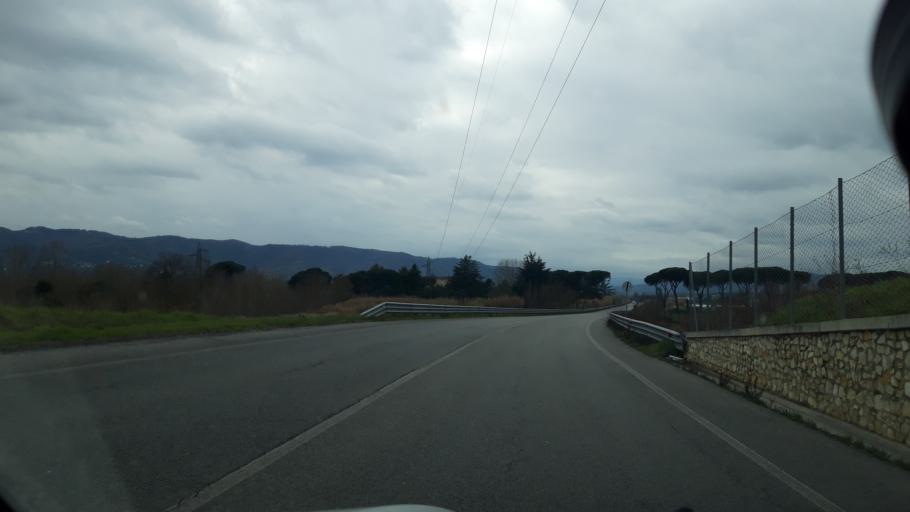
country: IT
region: Umbria
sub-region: Provincia di Perugia
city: Fontignano
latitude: 43.0096
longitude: 12.1938
